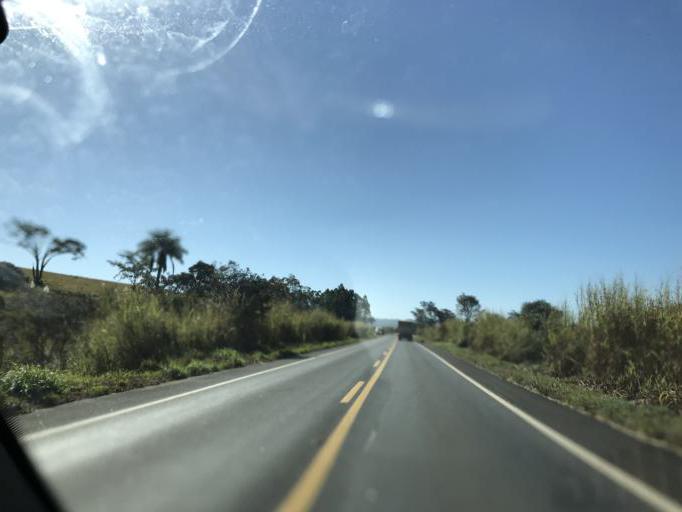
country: BR
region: Minas Gerais
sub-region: Bambui
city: Bambui
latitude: -19.8583
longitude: -45.9865
